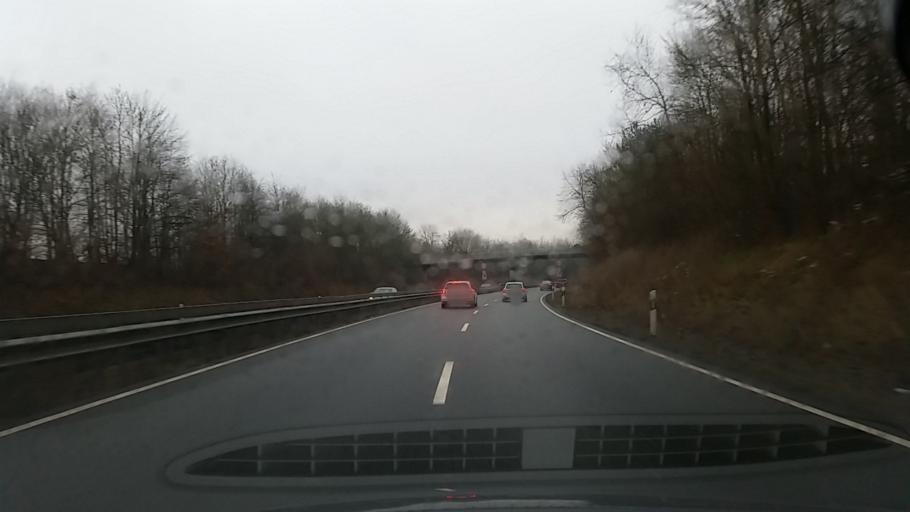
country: DE
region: Lower Saxony
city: Adendorf
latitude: 53.2645
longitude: 10.4366
